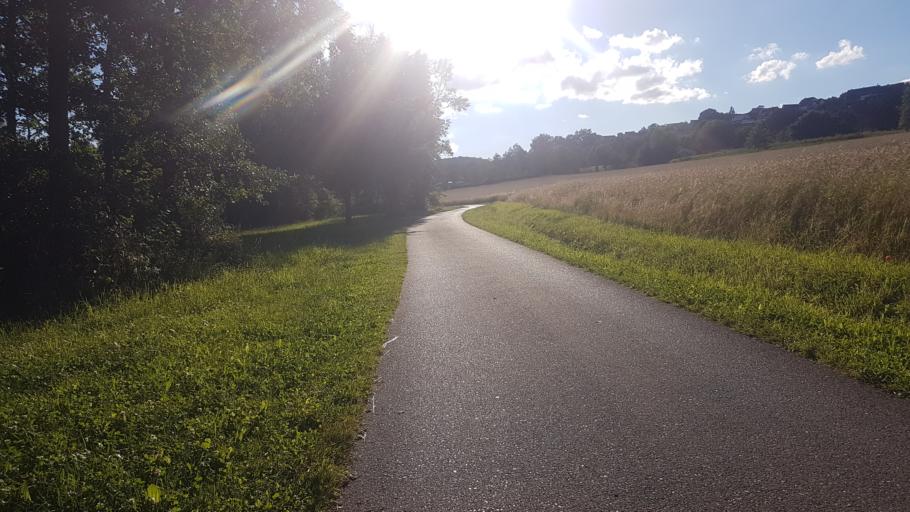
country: DE
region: Bavaria
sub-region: Regierungsbezirk Mittelfranken
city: Absberg
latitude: 49.1414
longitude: 10.8800
